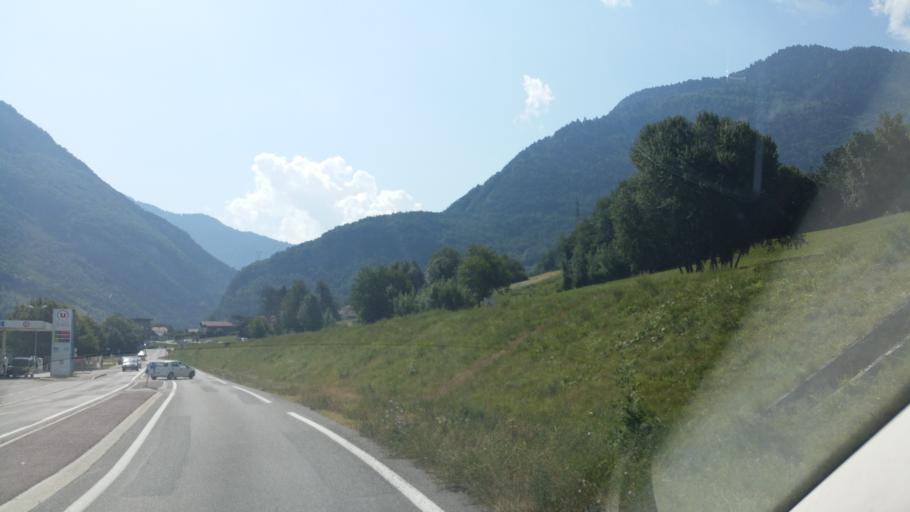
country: FR
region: Rhone-Alpes
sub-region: Departement de la Savoie
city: Aigueblanche
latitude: 45.5033
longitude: 6.4993
